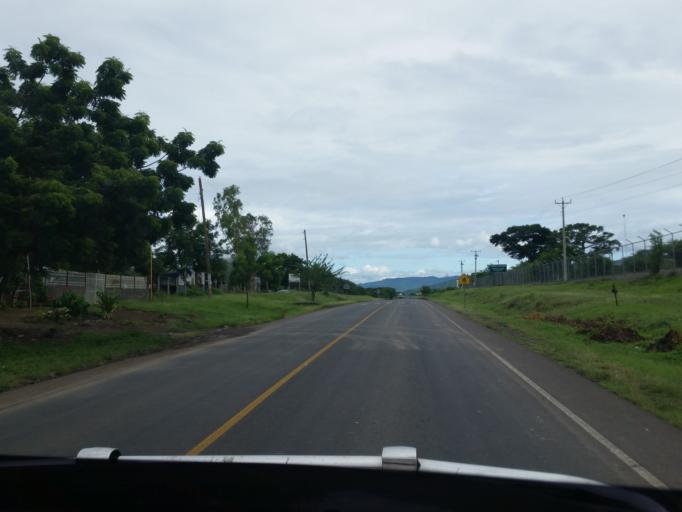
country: NI
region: Managua
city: Tipitapa
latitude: 12.3598
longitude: -86.0483
